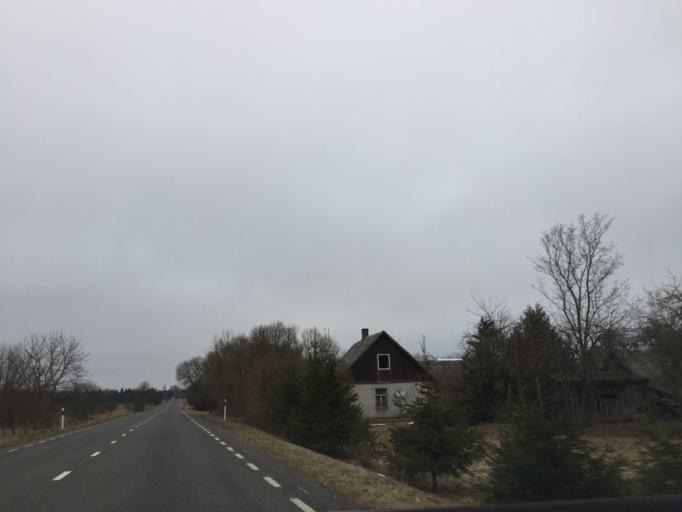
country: EE
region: Saare
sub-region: Kuressaare linn
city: Kuressaare
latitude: 58.5328
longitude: 22.3408
